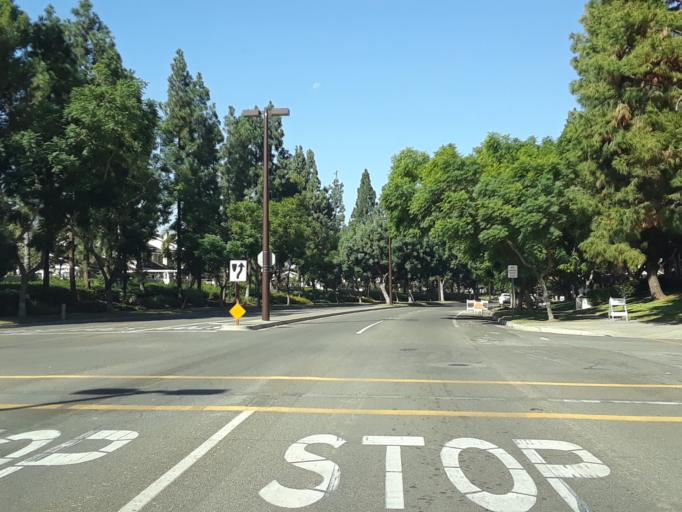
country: US
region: California
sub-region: Orange County
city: Irvine
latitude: 33.6684
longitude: -117.8108
